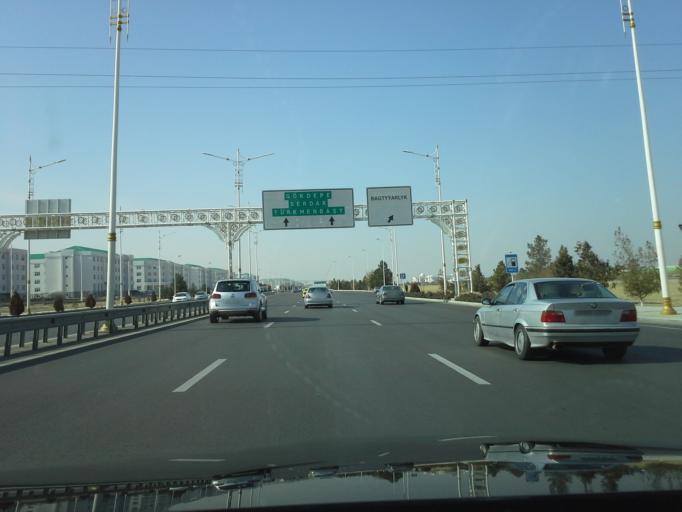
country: TM
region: Ahal
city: Ashgabat
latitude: 37.9806
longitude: 58.3376
